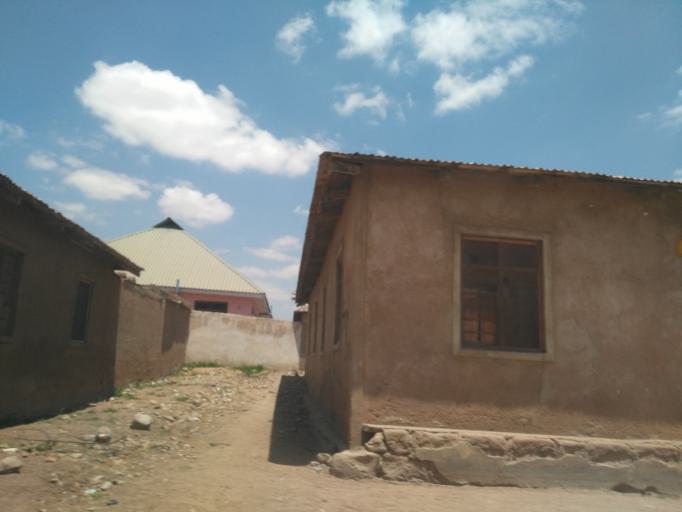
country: TZ
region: Dodoma
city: Dodoma
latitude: -6.1728
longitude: 35.7481
